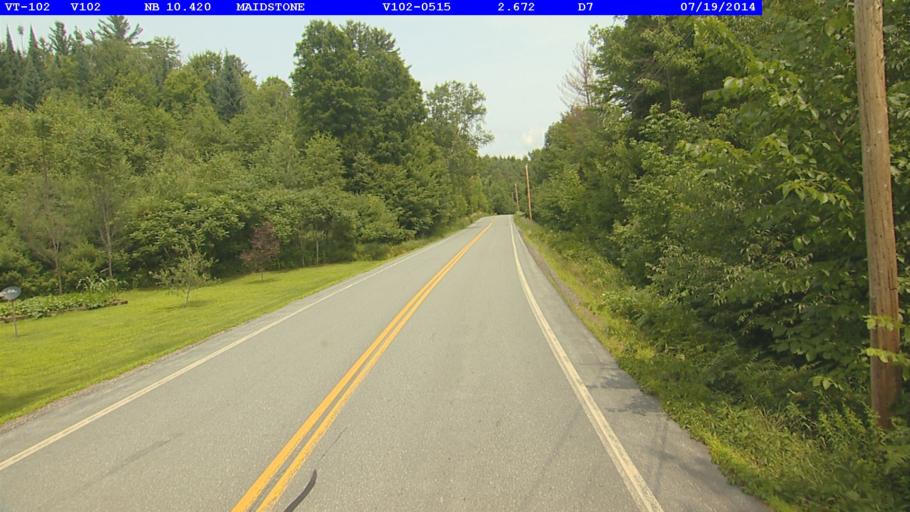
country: US
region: Vermont
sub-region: Essex County
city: Guildhall
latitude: 44.6016
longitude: -71.5635
